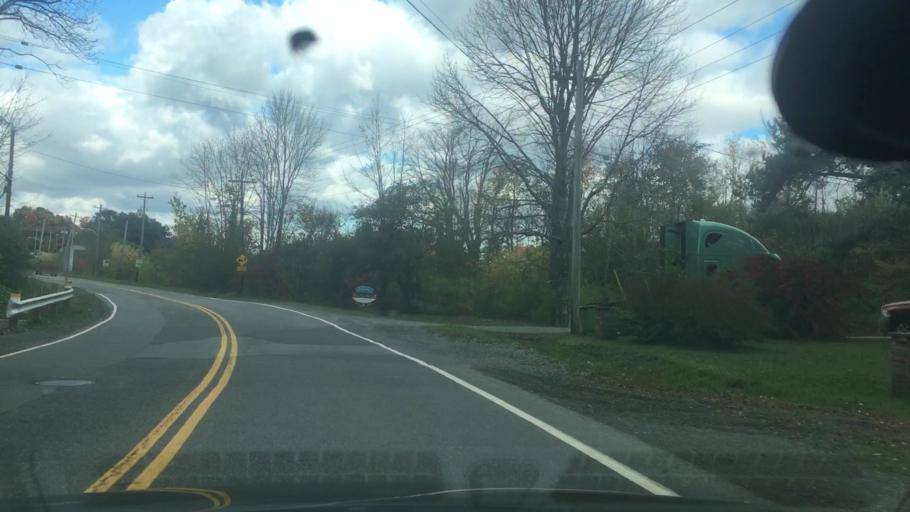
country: CA
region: Nova Scotia
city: Windsor
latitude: 44.9758
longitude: -64.1190
